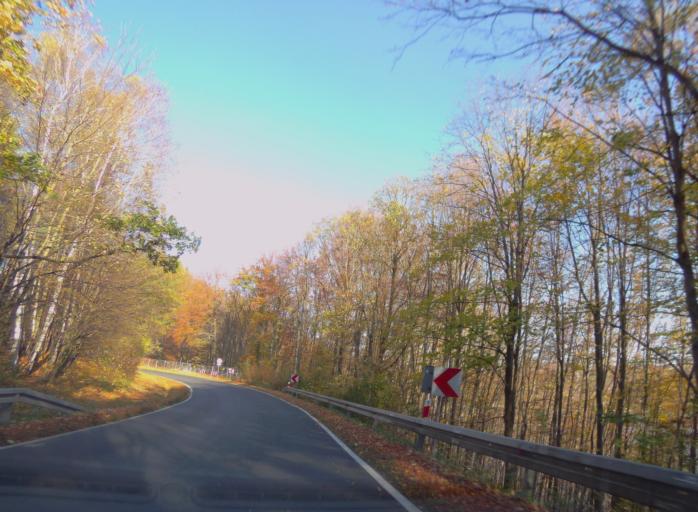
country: PL
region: Subcarpathian Voivodeship
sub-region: Powiat leski
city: Polanczyk
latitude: 49.3948
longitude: 22.4371
